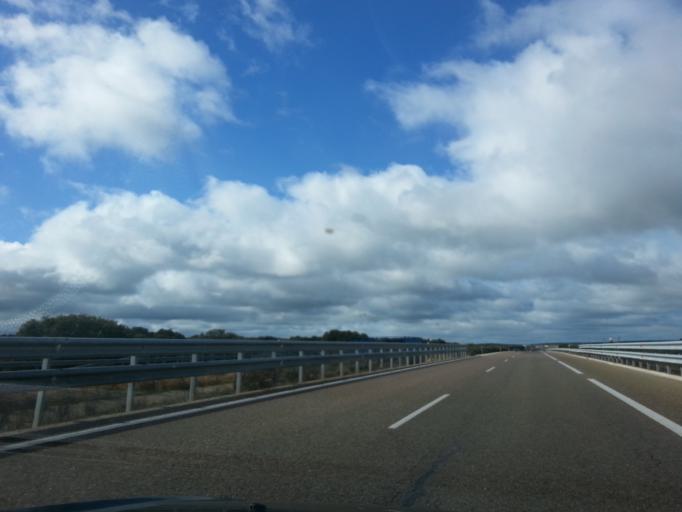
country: ES
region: Castille and Leon
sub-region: Provincia de Salamanca
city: Aldehuela de la Boveda
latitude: 40.8602
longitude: -6.0233
